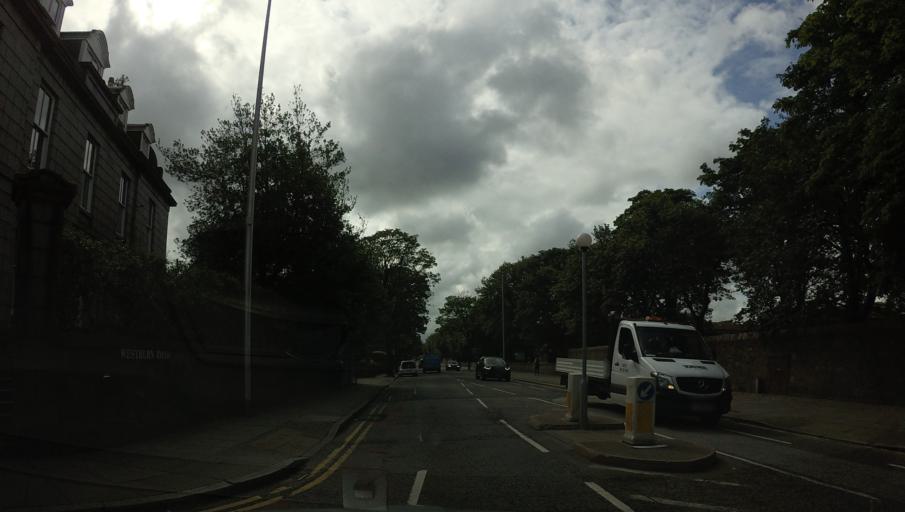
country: GB
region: Scotland
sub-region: Aberdeen City
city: Aberdeen
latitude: 57.1531
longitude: -2.1142
